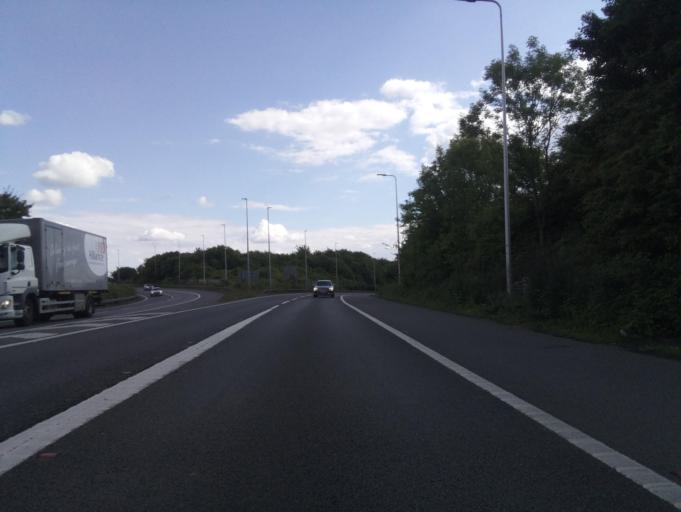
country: GB
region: England
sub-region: Hertfordshire
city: Abbots Langley
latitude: 51.7185
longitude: -0.3870
